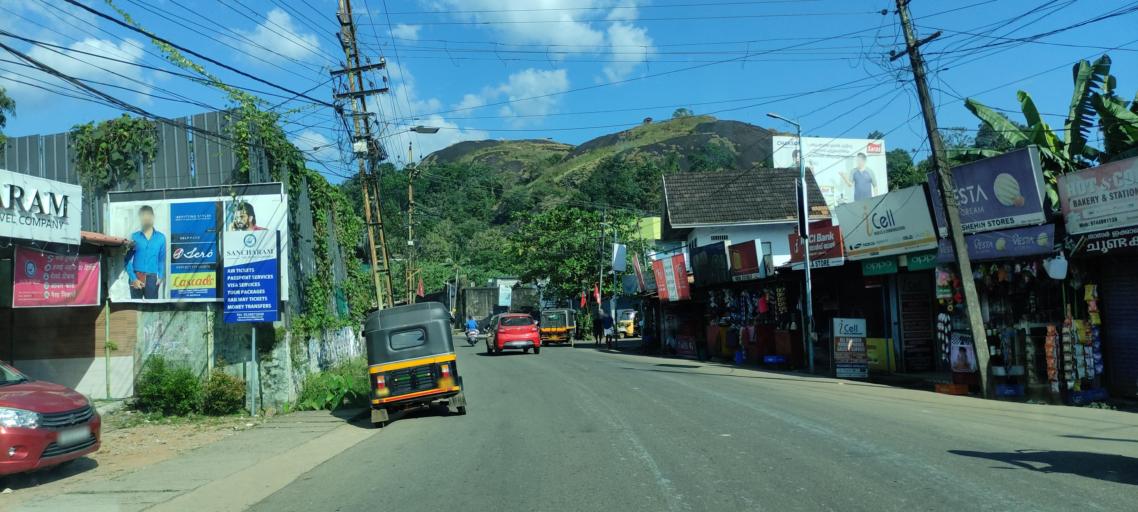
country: IN
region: Kerala
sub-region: Pattanamtitta
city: Pathanamthitta
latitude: 9.2648
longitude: 76.7914
